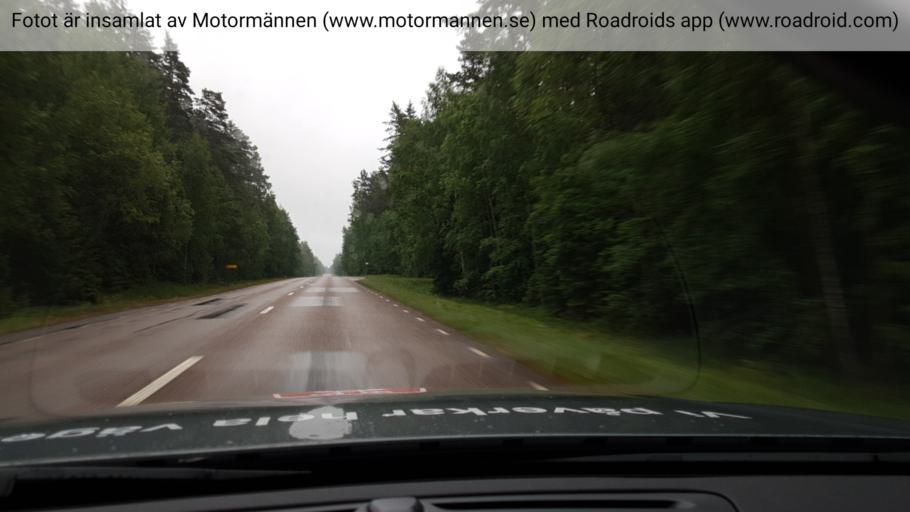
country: SE
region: Dalarna
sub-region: Avesta Kommun
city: Avesta
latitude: 59.9717
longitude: 16.1582
